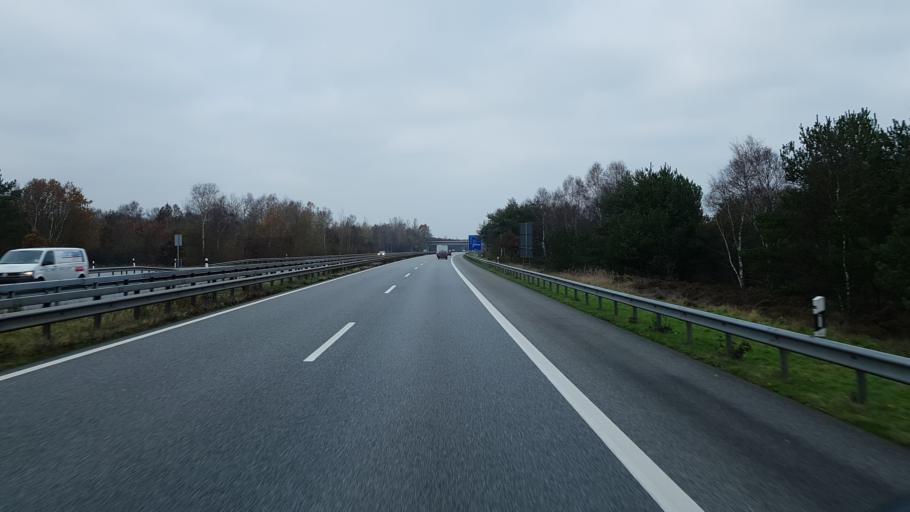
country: DE
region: Lower Saxony
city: Driftsethe
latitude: 53.3594
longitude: 8.5855
